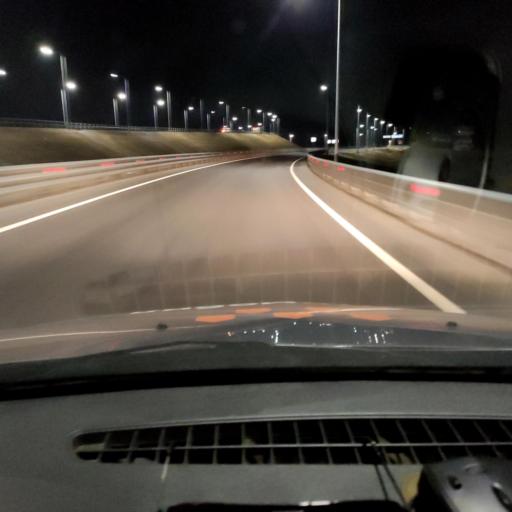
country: RU
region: Voronezj
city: Podgornoye
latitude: 51.8355
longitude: 39.2147
